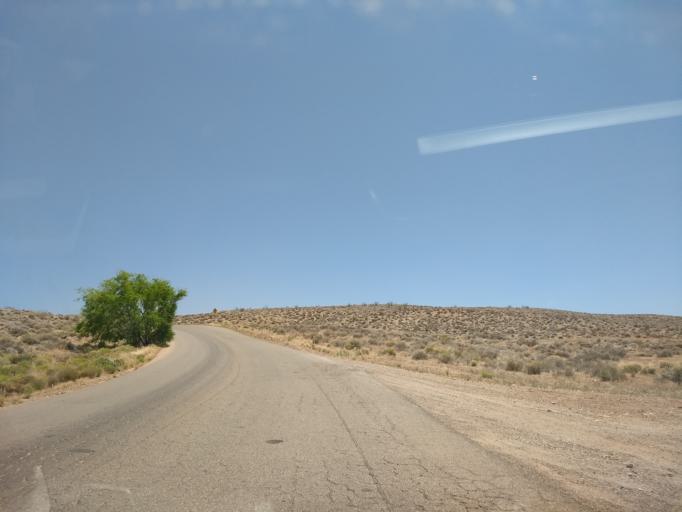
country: US
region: Utah
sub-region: Washington County
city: Washington
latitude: 37.1356
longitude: -113.4629
